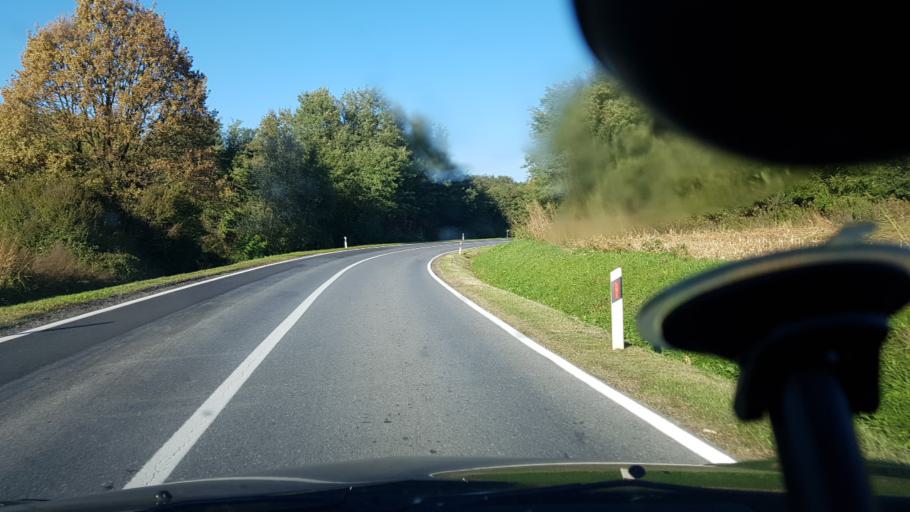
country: HR
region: Koprivnicko-Krizevacka
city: Virje
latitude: 46.0216
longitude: 16.9738
